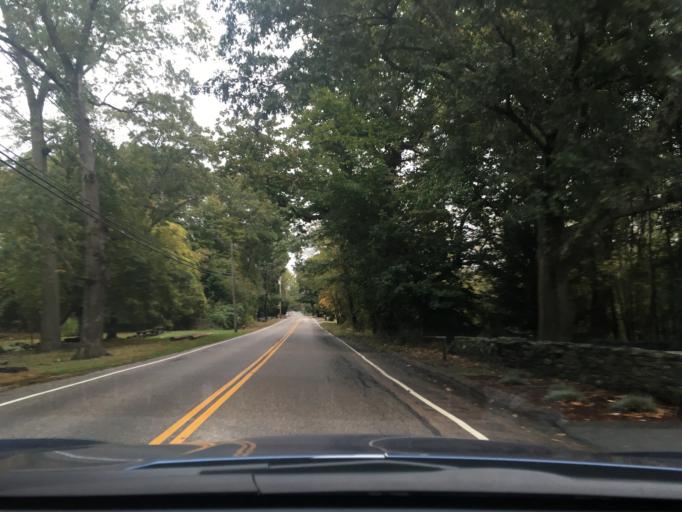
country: US
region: Rhode Island
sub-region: Kent County
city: East Greenwich
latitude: 41.6361
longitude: -71.4354
